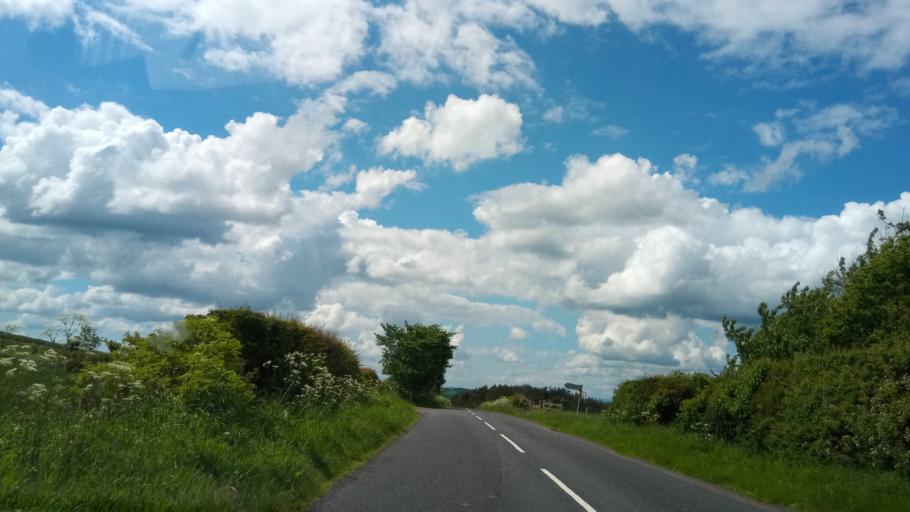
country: GB
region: Scotland
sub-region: The Scottish Borders
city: Coldstream
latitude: 55.6042
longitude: -2.2653
